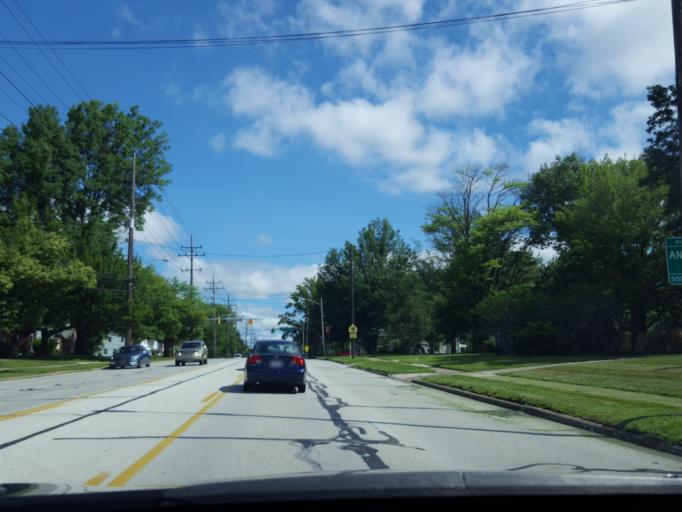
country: US
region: Ohio
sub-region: Cuyahoga County
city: Lyndhurst
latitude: 41.5342
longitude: -81.4969
